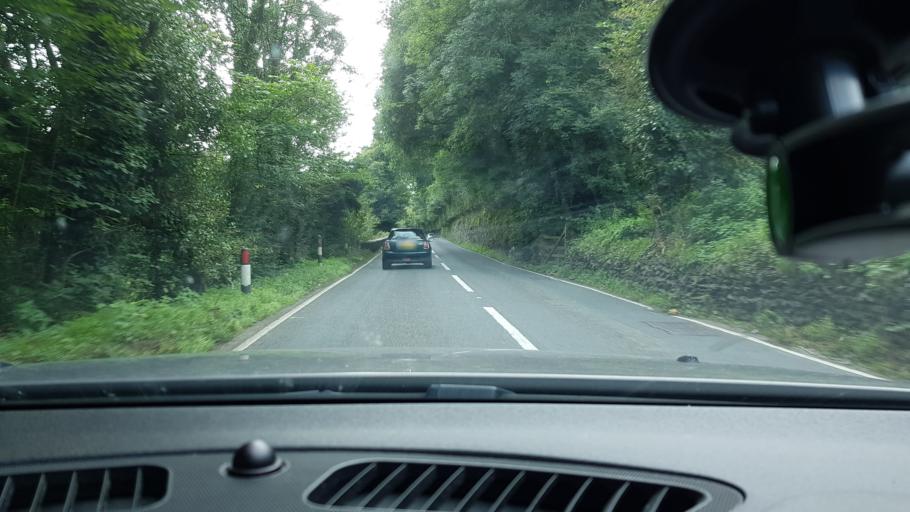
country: GB
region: England
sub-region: Cornwall
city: Helland
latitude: 50.5615
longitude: -4.7560
